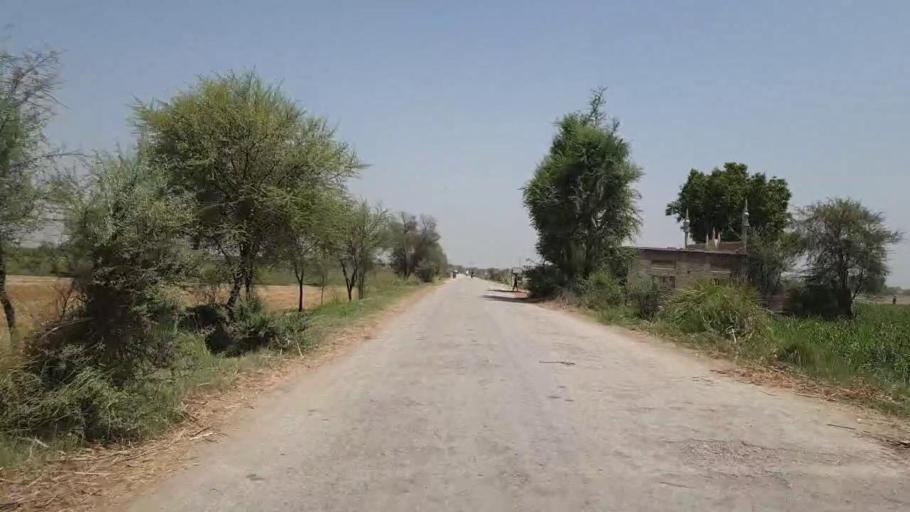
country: PK
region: Sindh
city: Adilpur
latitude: 27.8766
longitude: 69.2860
